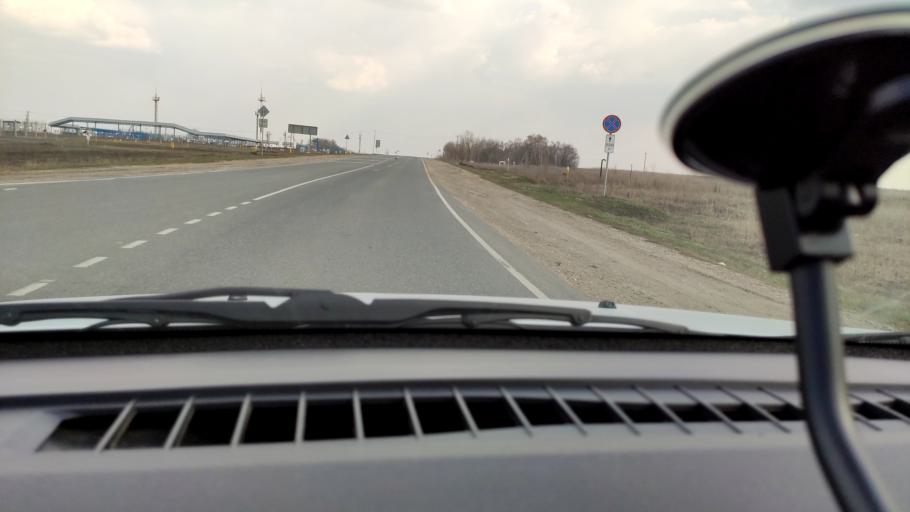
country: RU
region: Samara
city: Dubovyy Umet
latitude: 53.0831
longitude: 50.3439
